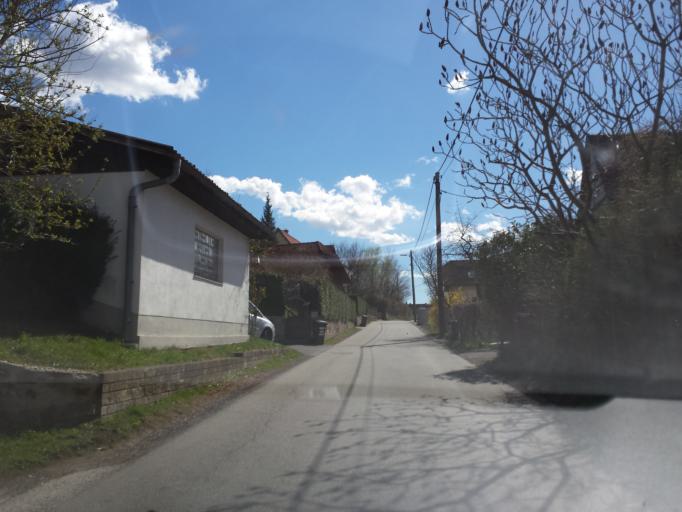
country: AT
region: Styria
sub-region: Politischer Bezirk Graz-Umgebung
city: Stattegg
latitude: 47.1208
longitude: 15.4291
